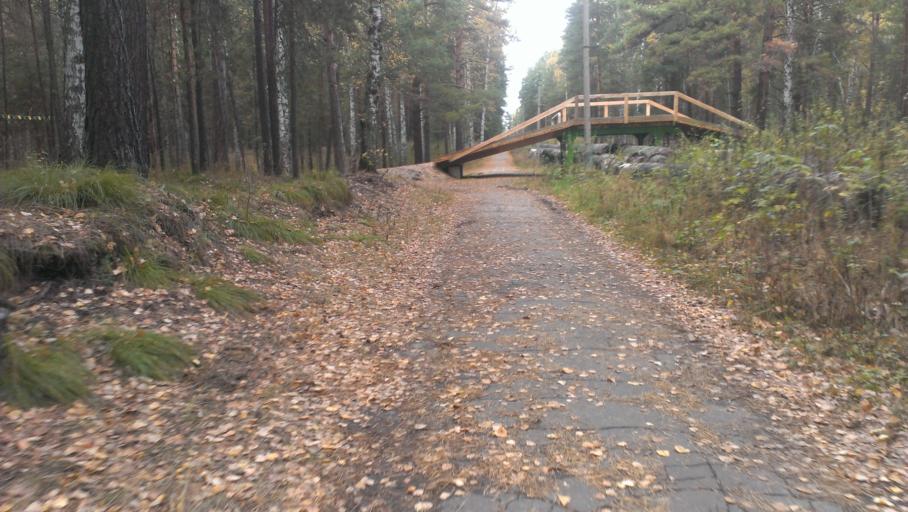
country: RU
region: Altai Krai
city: Yuzhnyy
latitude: 53.2644
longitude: 83.6854
